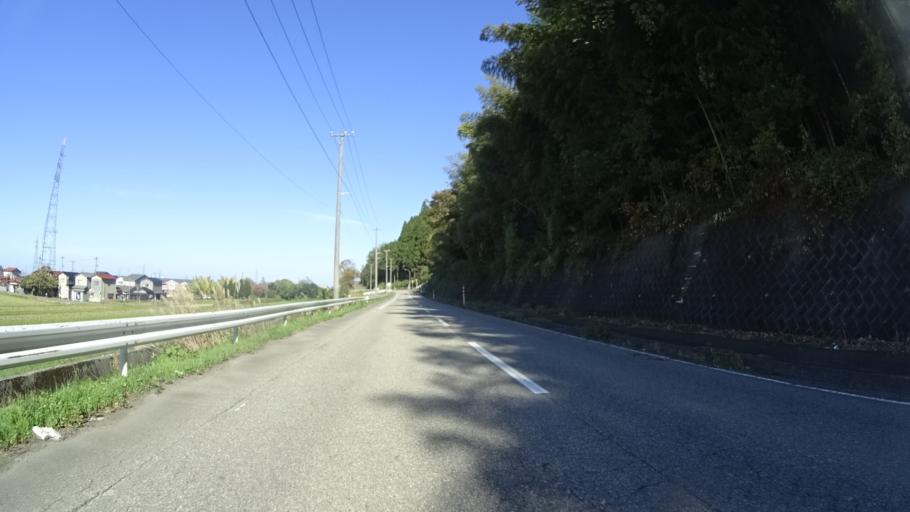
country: JP
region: Ishikawa
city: Tsurugi-asahimachi
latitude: 36.4796
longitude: 136.6161
